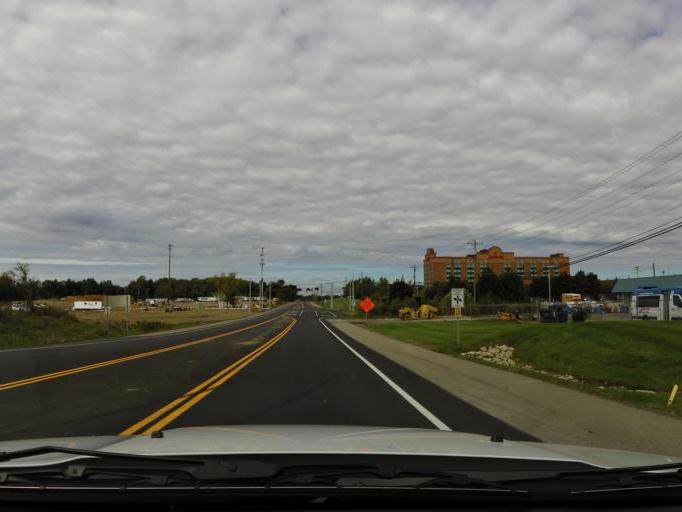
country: US
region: Ohio
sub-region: Hamilton County
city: Delhi Hills
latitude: 39.0741
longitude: -84.6541
